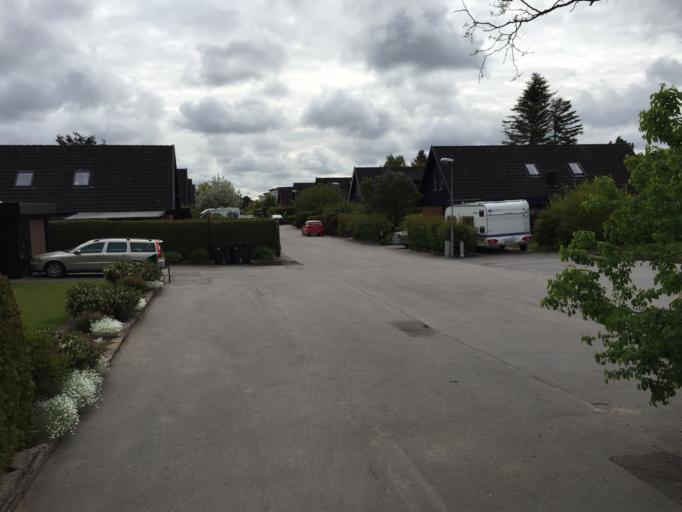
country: SE
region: Skane
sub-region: Lunds Kommun
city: Veberod
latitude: 55.6284
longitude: 13.4958
